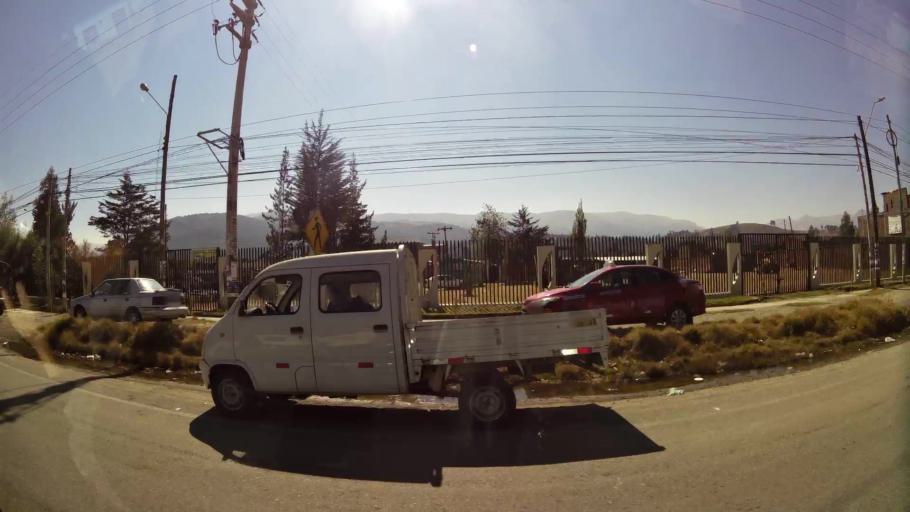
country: PE
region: Junin
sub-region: Provincia de Huancayo
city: San Agustin
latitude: -11.9989
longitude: -75.2531
